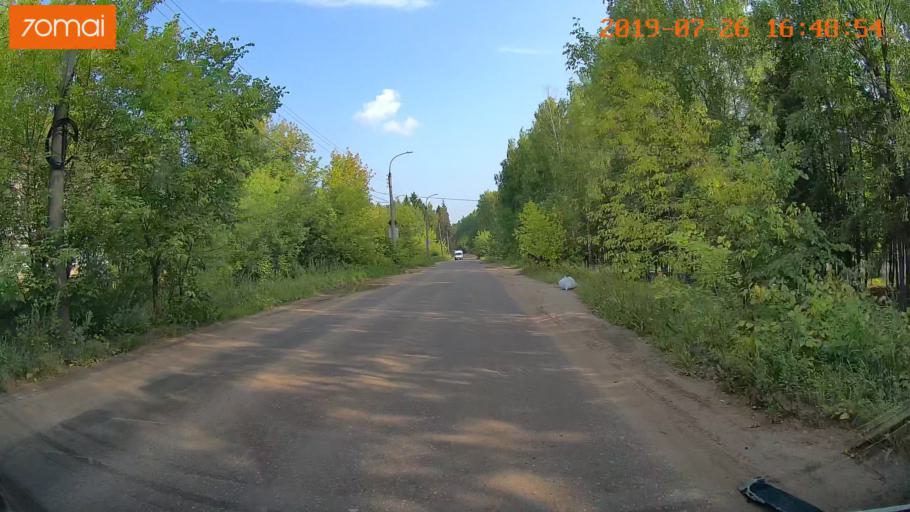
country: RU
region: Ivanovo
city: Bogorodskoye
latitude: 57.0326
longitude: 41.0174
